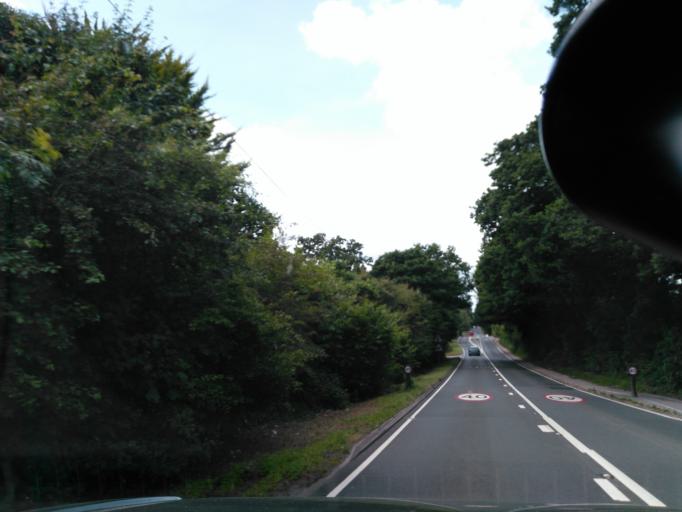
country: GB
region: England
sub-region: Hampshire
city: West Wellow
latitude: 50.9713
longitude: -1.5932
